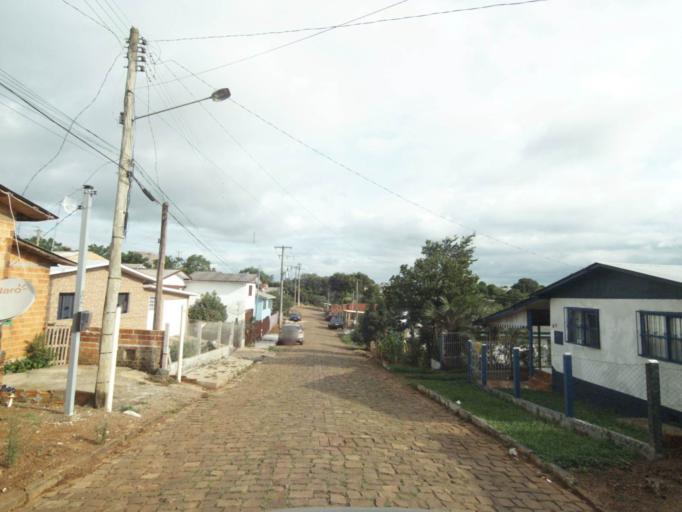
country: BR
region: Rio Grande do Sul
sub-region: Lagoa Vermelha
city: Lagoa Vermelha
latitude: -28.2045
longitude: -51.5344
